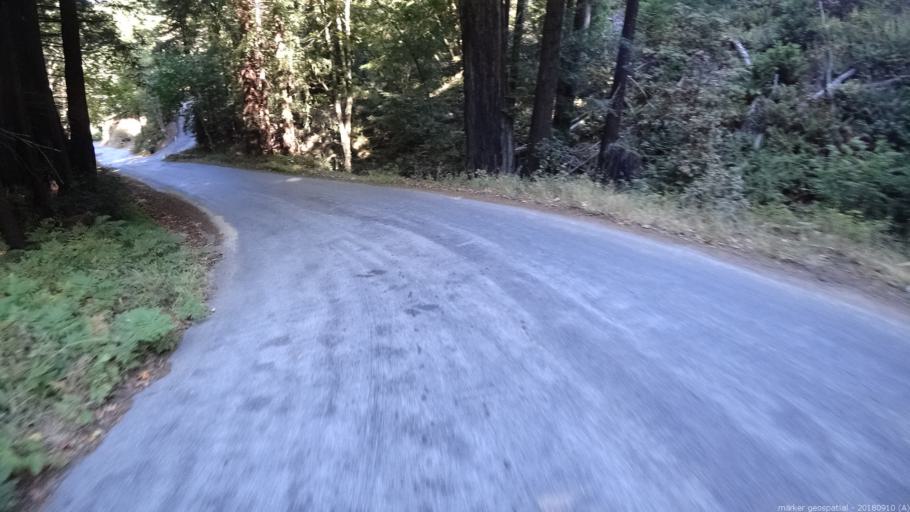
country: US
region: California
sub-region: Monterey County
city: Carmel Valley Village
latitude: 36.3898
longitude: -121.8716
